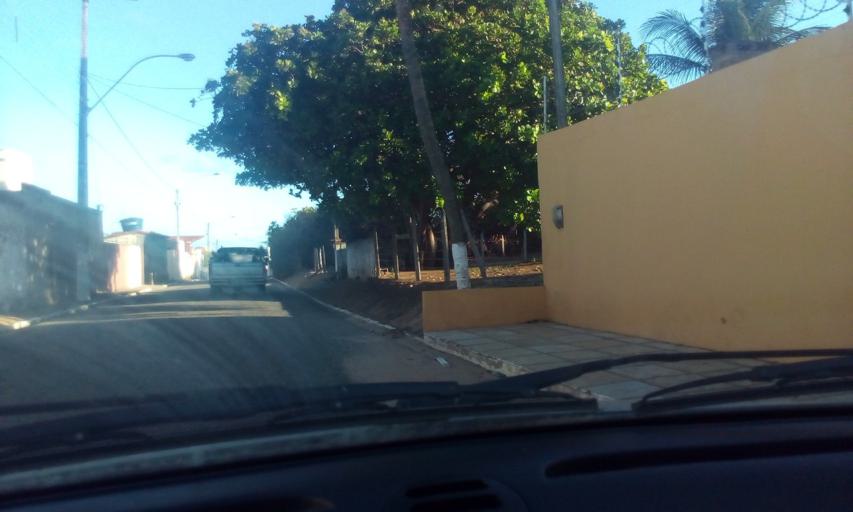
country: BR
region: Rio Grande do Norte
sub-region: Parnamirim
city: Parnamirim
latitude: -5.9602
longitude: -35.1501
